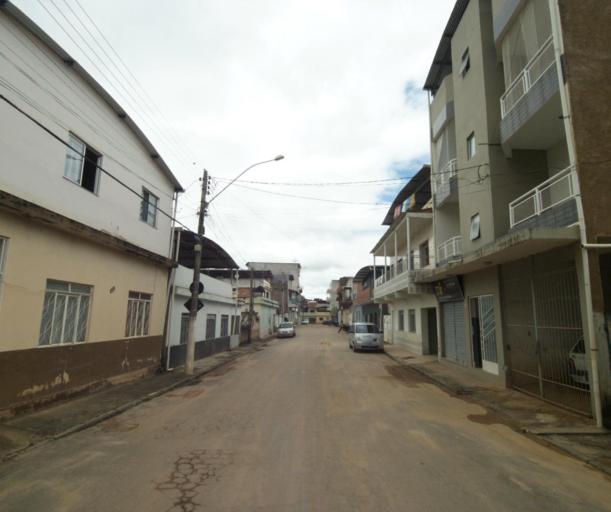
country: BR
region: Espirito Santo
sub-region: Irupi
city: Irupi
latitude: -20.3442
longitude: -41.6403
